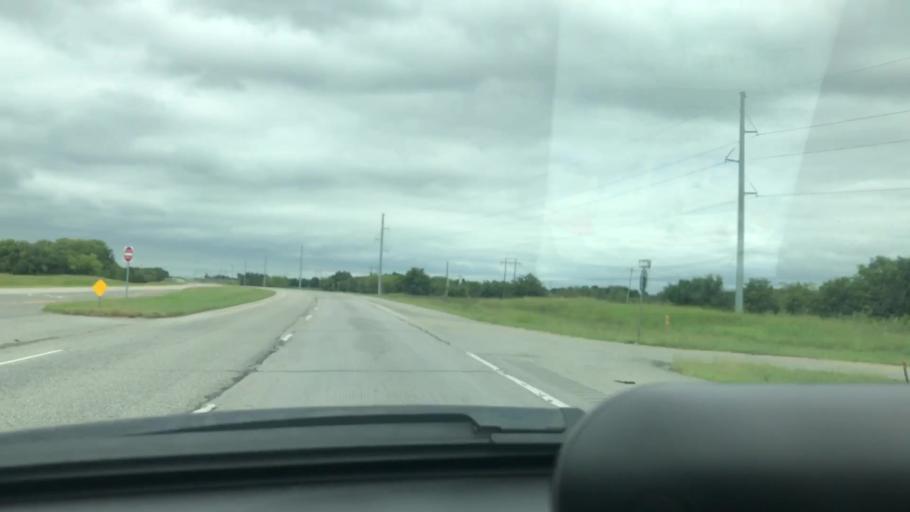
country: US
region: Oklahoma
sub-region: Wagoner County
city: Wagoner
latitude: 35.9973
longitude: -95.3689
